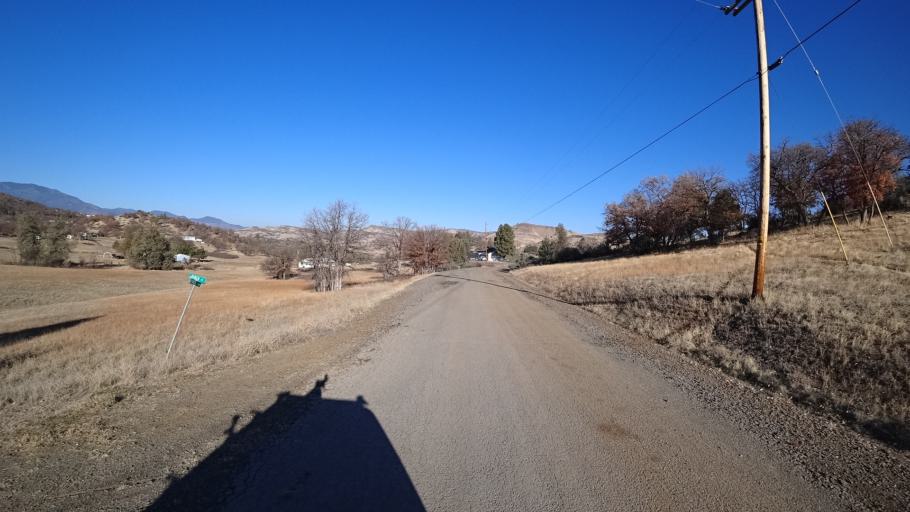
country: US
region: California
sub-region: Siskiyou County
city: Montague
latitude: 41.8895
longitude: -122.4887
